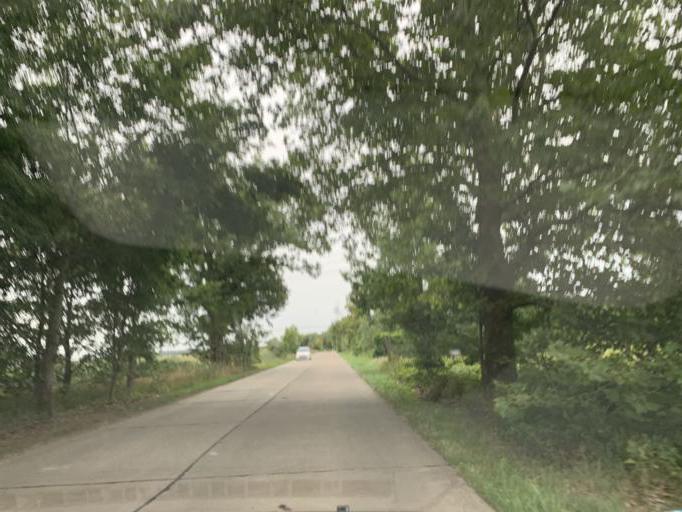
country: DE
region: Brandenburg
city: Zehdenick
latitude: 52.9982
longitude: 13.2656
